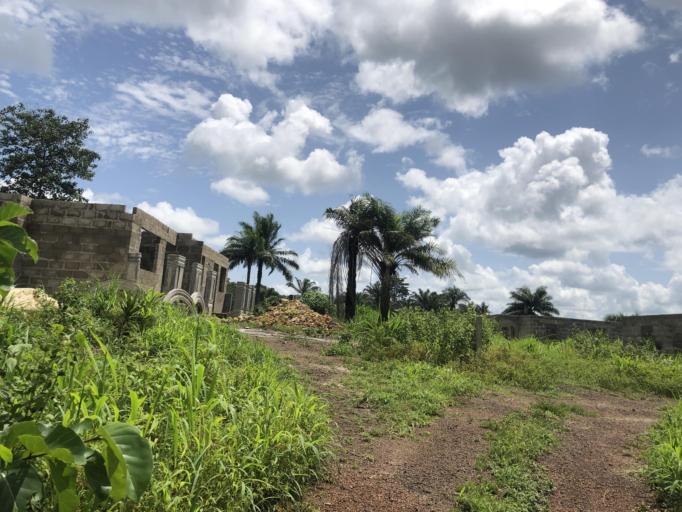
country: SL
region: Northern Province
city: Magburaka
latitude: 8.7111
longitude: -11.9292
